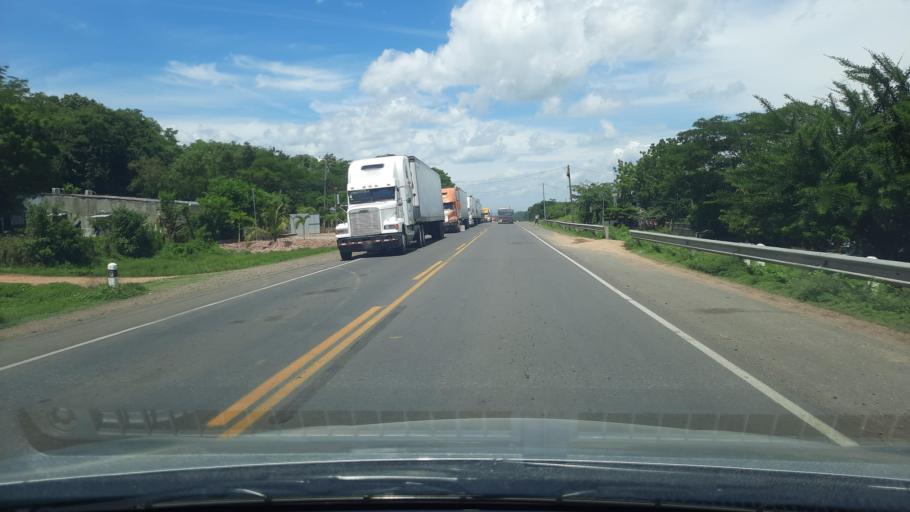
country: NI
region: Chinandega
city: Somotillo
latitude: 13.0577
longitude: -86.9255
